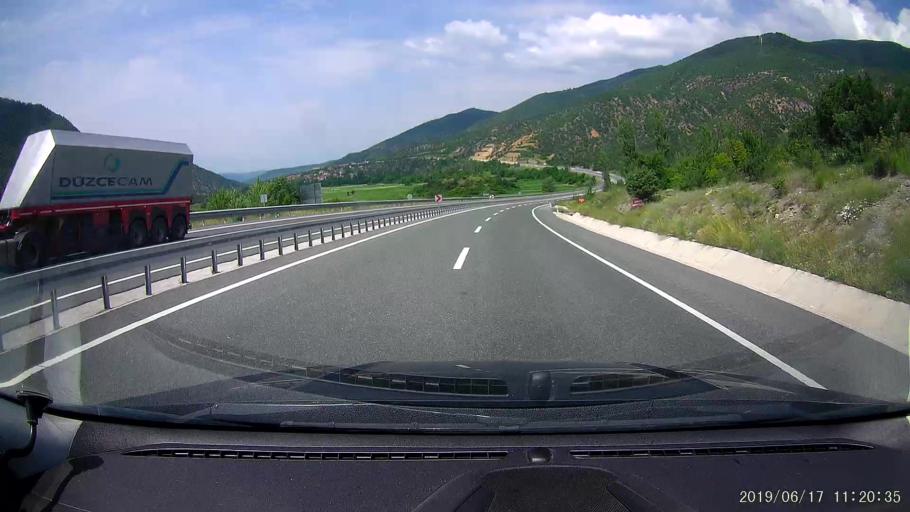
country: TR
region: Cankiri
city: Yaprakli
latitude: 40.9114
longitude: 33.8036
